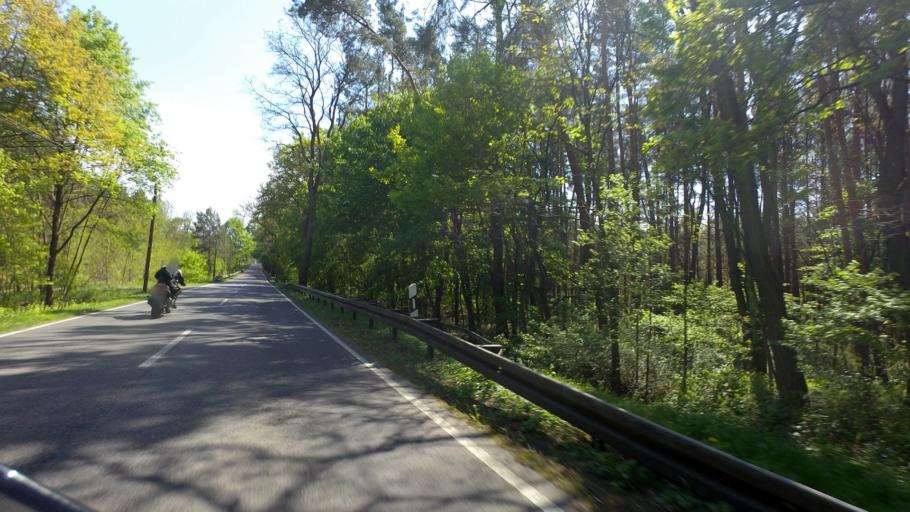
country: DE
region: Brandenburg
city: Lieberose
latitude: 52.0066
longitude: 14.1918
